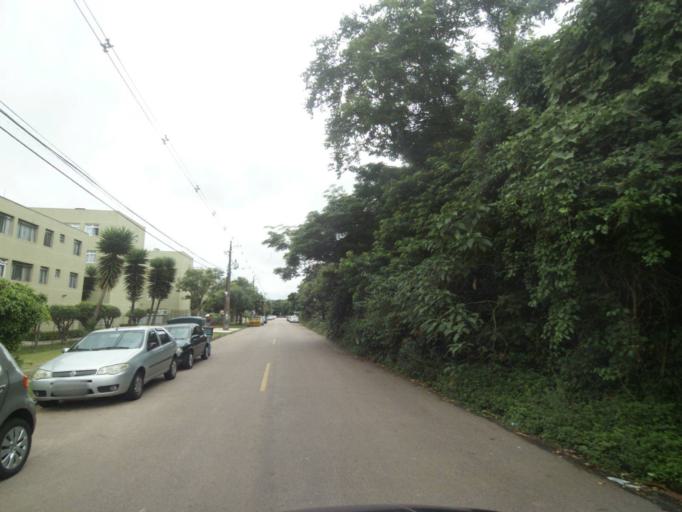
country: BR
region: Parana
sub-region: Curitiba
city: Curitiba
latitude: -25.4754
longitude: -49.3322
